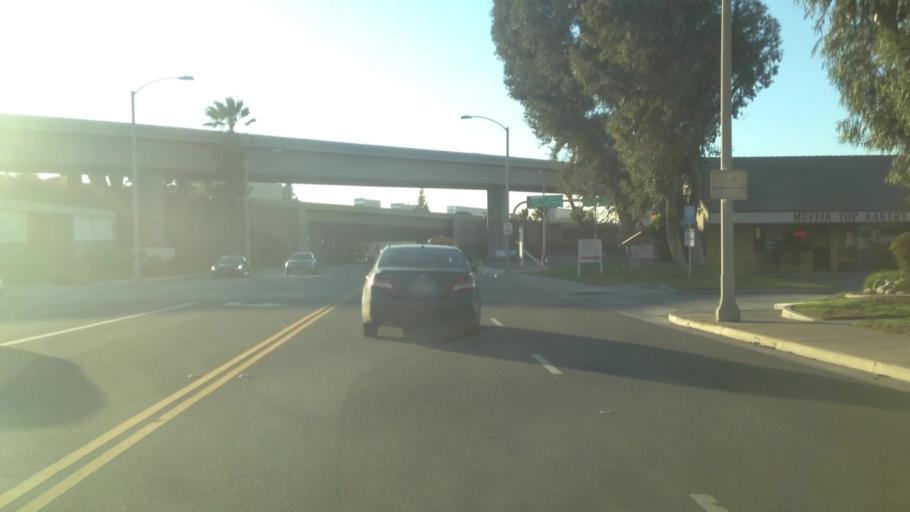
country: US
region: California
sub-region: Riverside County
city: Highgrove
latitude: 33.9903
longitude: -117.3488
